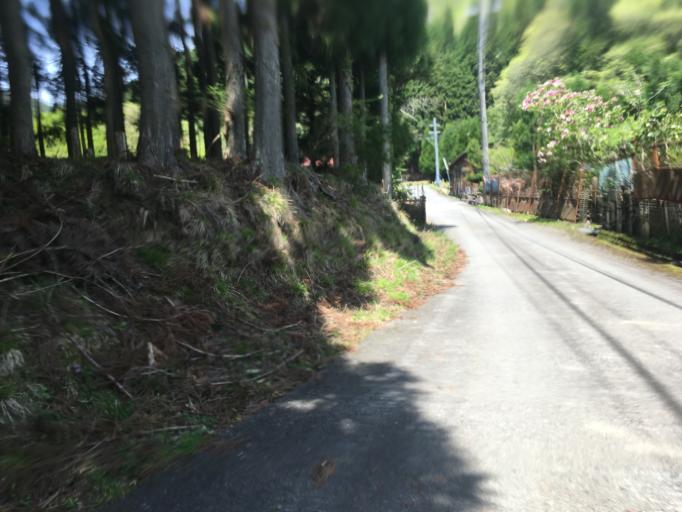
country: JP
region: Kyoto
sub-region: Kyoto-shi
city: Kamigyo-ku
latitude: 35.1258
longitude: 135.6995
